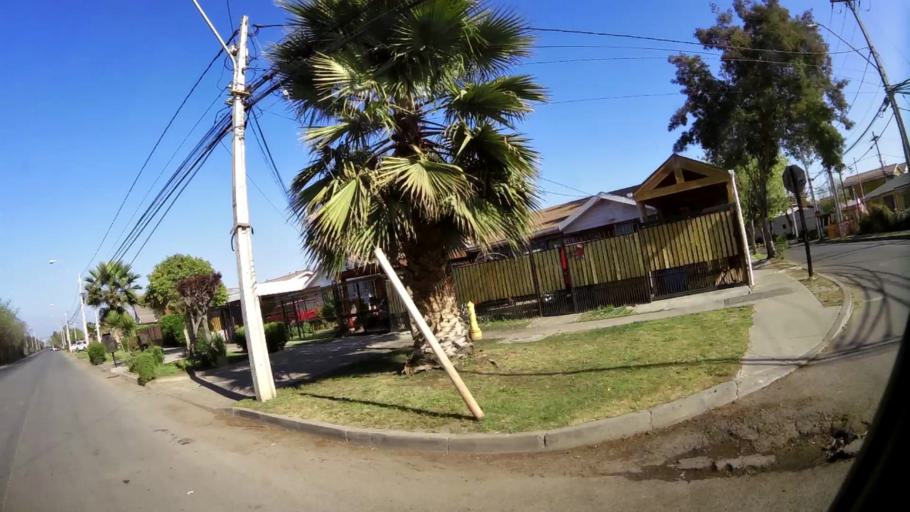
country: CL
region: Santiago Metropolitan
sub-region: Provincia de Santiago
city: Lo Prado
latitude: -33.4881
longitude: -70.7787
